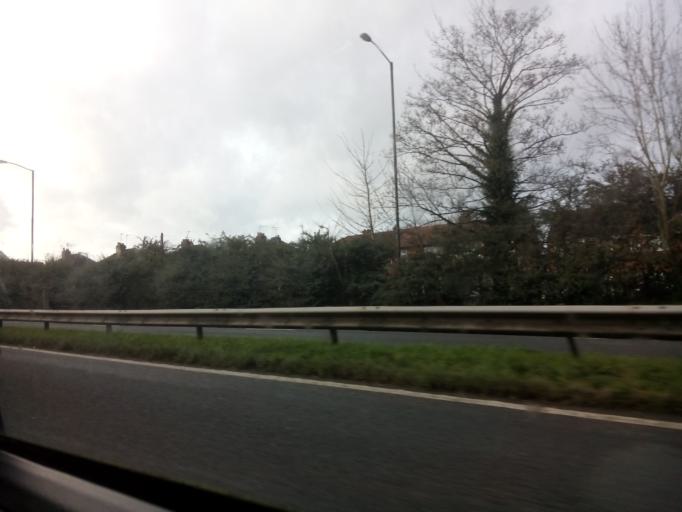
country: GB
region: England
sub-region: Worcestershire
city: Barnt Green
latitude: 52.3952
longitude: -2.0217
